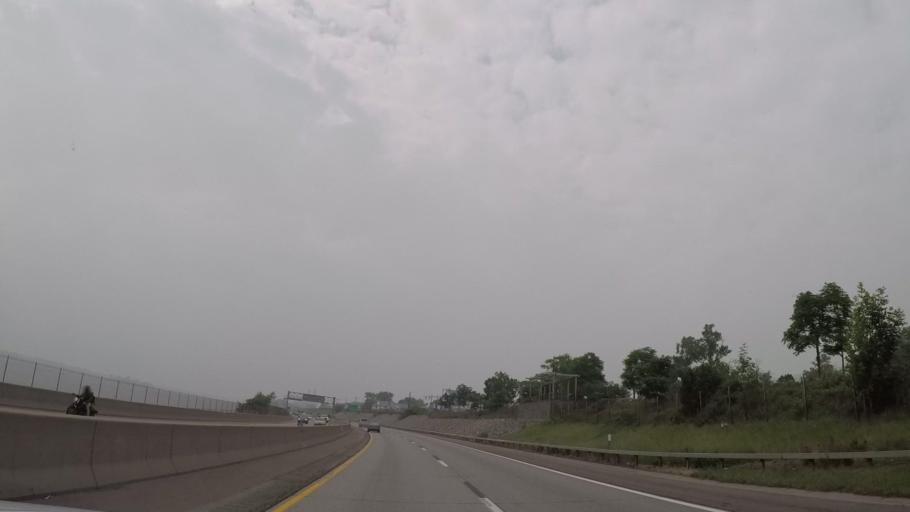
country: US
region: New York
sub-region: Erie County
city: Kenmore
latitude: 42.9552
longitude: -78.9111
